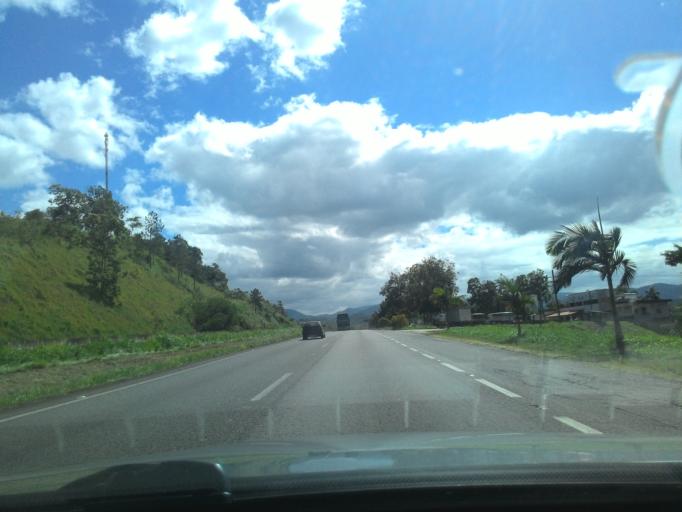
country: BR
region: Sao Paulo
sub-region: Cajati
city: Cajati
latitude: -24.7521
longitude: -48.1565
